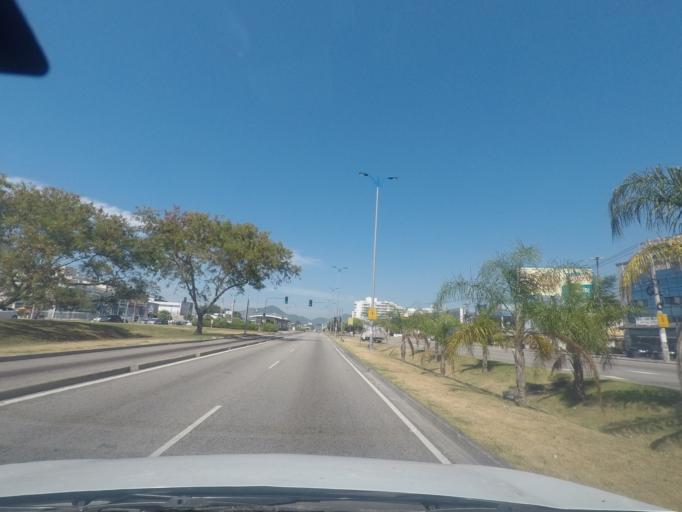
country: BR
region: Rio de Janeiro
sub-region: Nilopolis
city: Nilopolis
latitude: -23.0092
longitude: -43.4472
